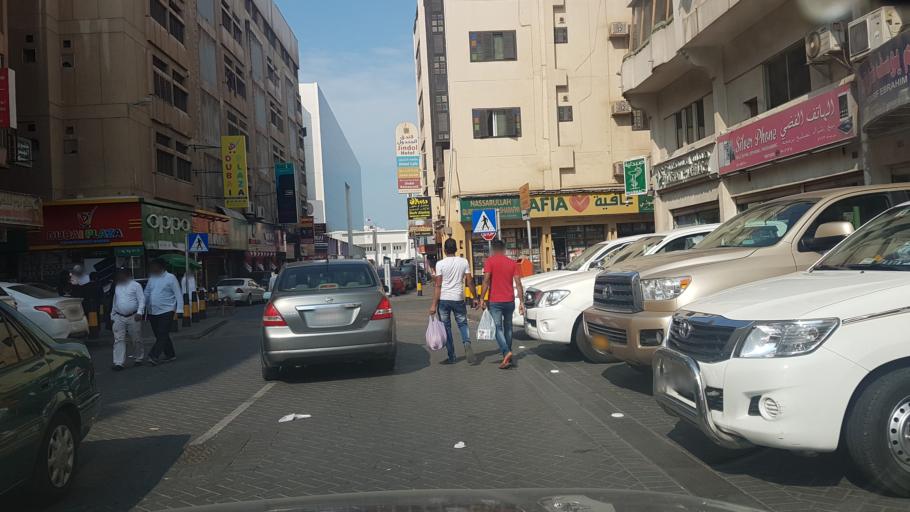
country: BH
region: Manama
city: Manama
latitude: 26.2313
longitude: 50.5741
